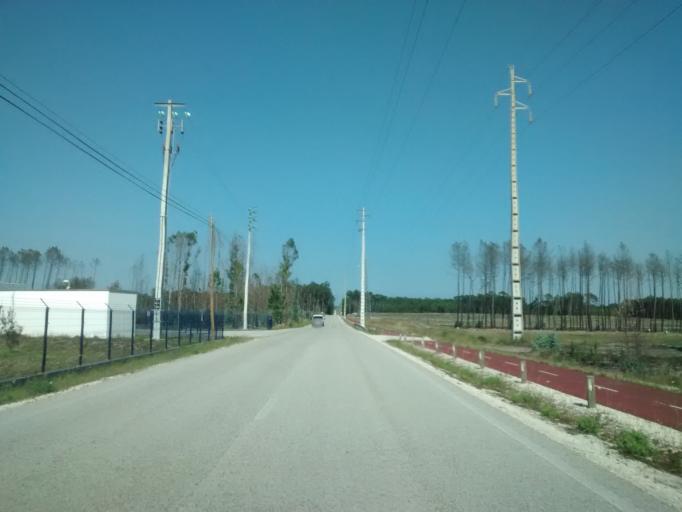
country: PT
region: Leiria
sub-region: Leiria
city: Monte Redondo
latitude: 39.9797
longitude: -8.8466
